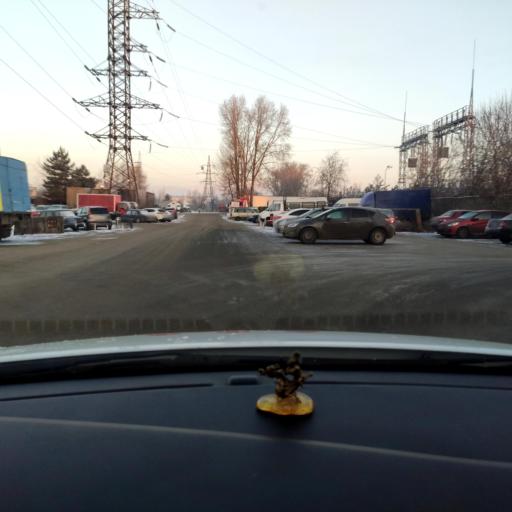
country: RU
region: Tatarstan
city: Staroye Arakchino
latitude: 55.8298
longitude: 49.0305
